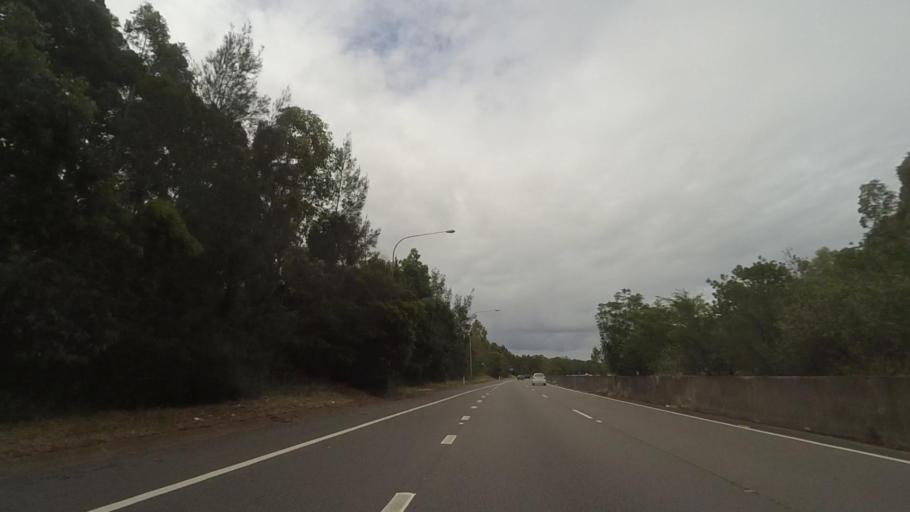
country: AU
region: New South Wales
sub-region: Port Stephens Shire
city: Raymond Terrace
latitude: -32.7501
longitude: 151.7670
